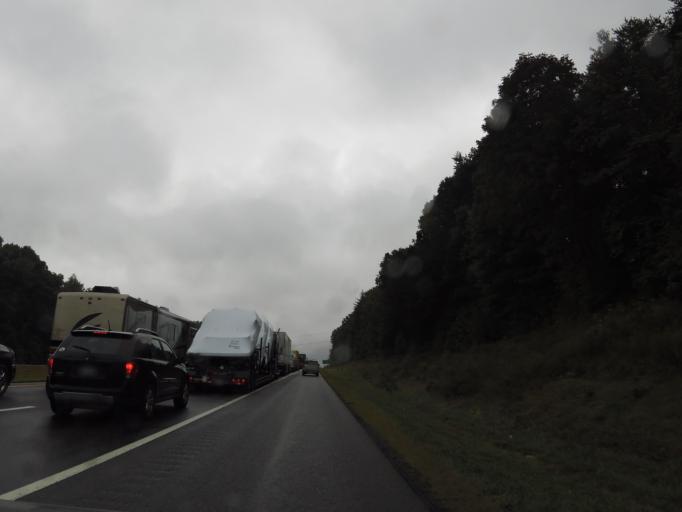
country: US
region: Tennessee
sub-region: Bradley County
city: Hopewell
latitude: 35.2199
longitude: -84.8617
